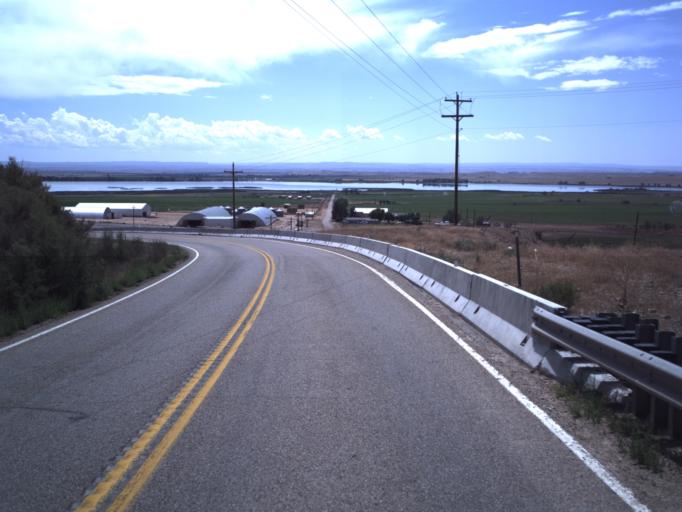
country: US
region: Utah
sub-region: Uintah County
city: Maeser
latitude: 40.2238
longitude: -109.6843
